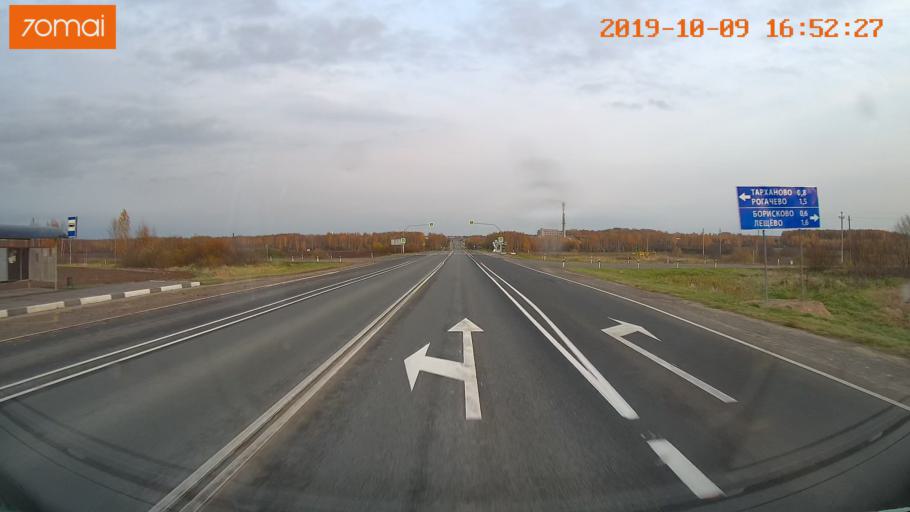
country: RU
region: Ivanovo
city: Privolzhsk
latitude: 57.3807
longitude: 41.2471
